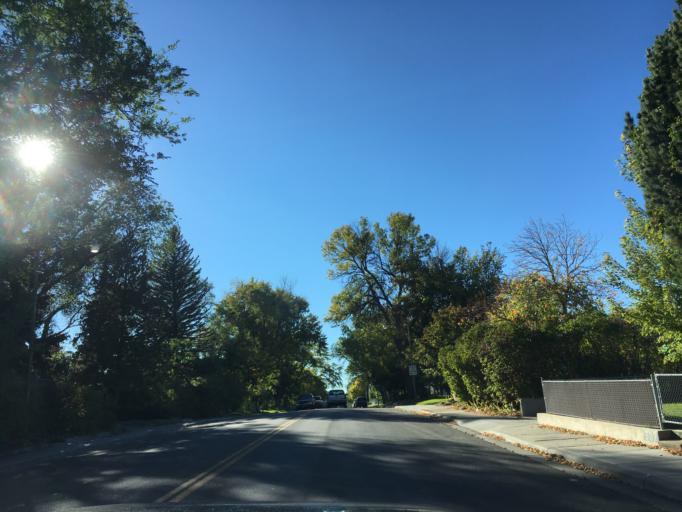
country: US
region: Montana
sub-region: Yellowstone County
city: Billings
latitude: 45.7899
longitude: -108.5283
